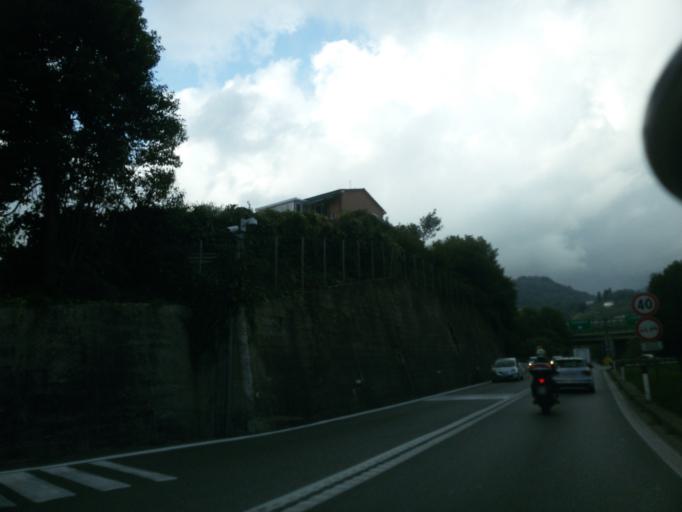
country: IT
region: Liguria
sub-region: Provincia di Genova
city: Rapallo
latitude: 44.3571
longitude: 9.2095
